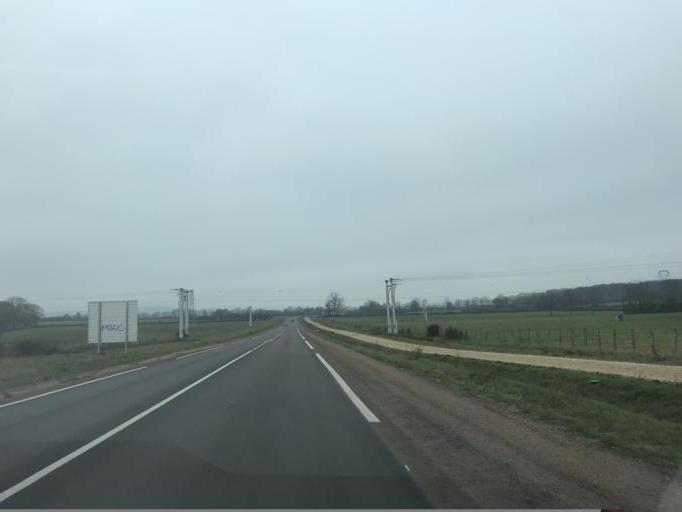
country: FR
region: Bourgogne
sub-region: Departement de l'Yonne
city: Avallon
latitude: 47.5007
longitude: 3.9256
